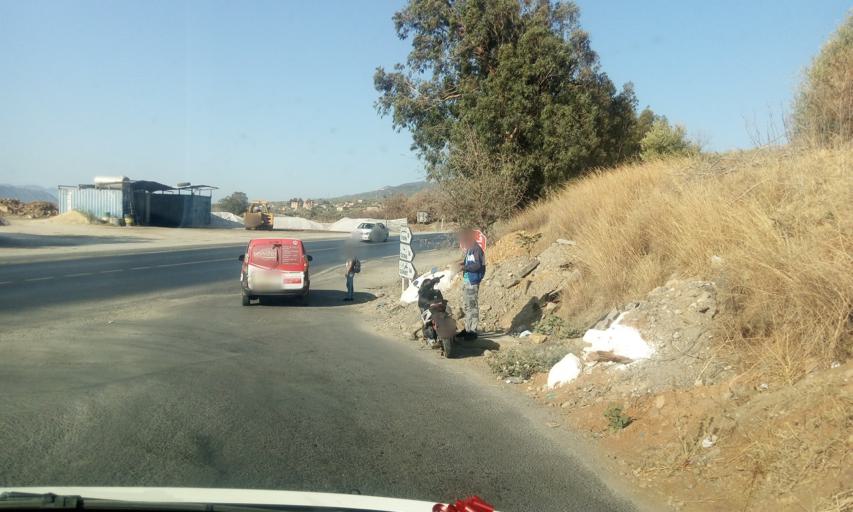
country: DZ
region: Tizi Ouzou
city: Chemini
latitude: 36.5690
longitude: 4.6418
